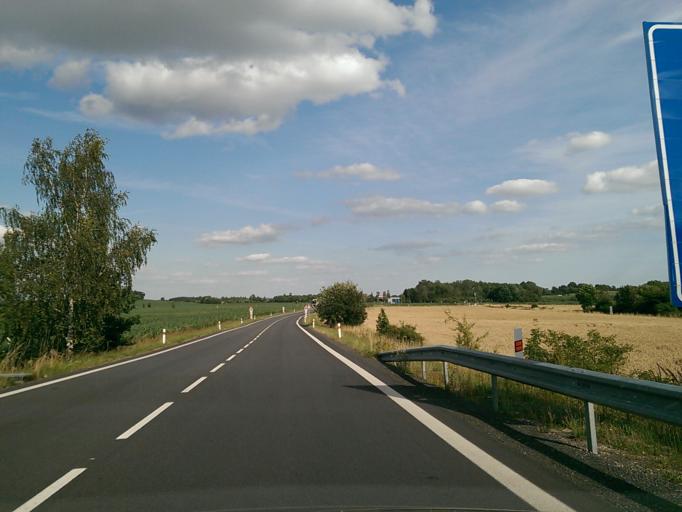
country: CZ
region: Central Bohemia
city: Bakov nad Jizerou
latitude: 50.4850
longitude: 14.9537
